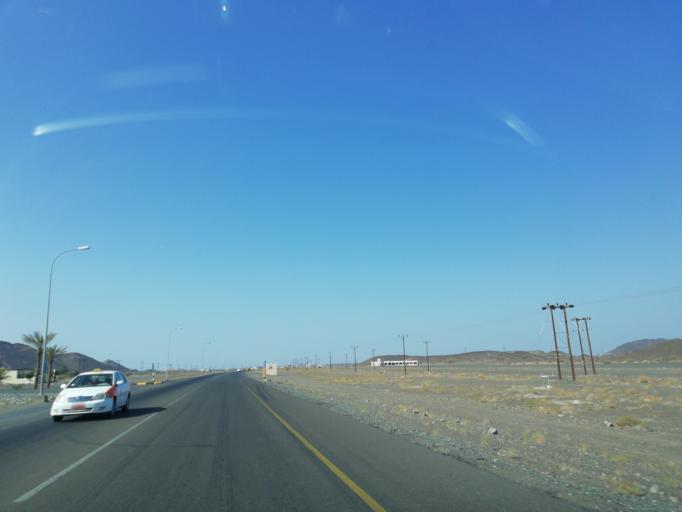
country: OM
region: Ash Sharqiyah
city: Ibra'
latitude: 22.7214
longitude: 58.1486
